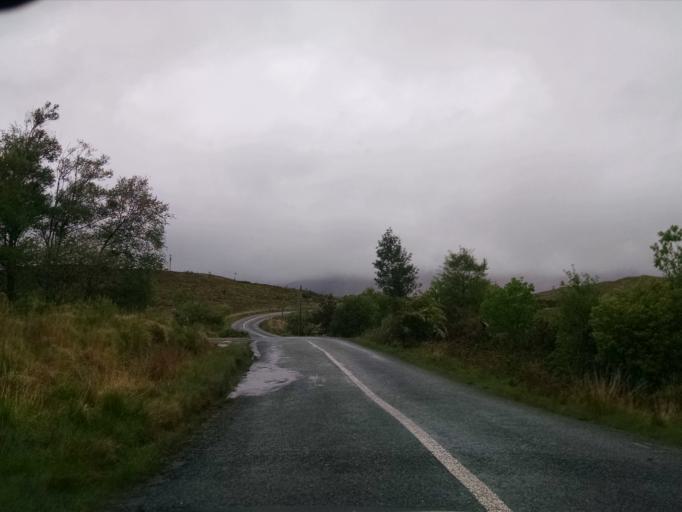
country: IE
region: Connaught
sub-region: County Galway
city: Clifden
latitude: 53.4864
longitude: -9.7398
